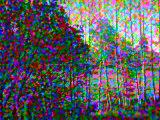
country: SE
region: Soedermanland
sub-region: Flens Kommun
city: Halleforsnas
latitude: 59.1610
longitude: 16.5133
